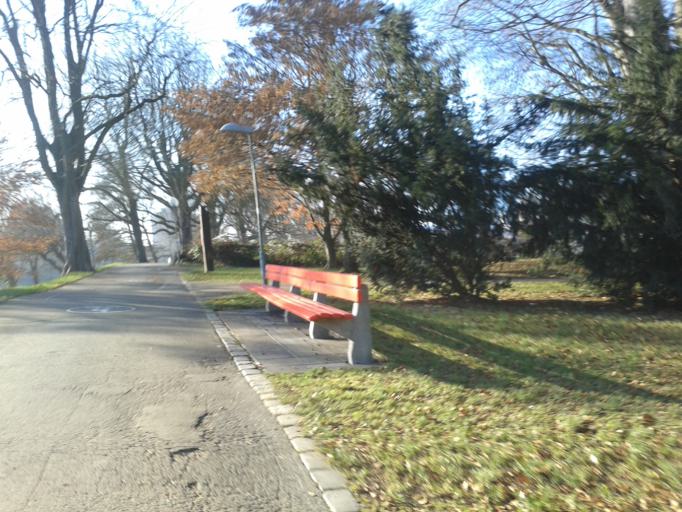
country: DE
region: Bavaria
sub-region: Swabia
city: Neu-Ulm
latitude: 48.4018
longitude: 10.0092
